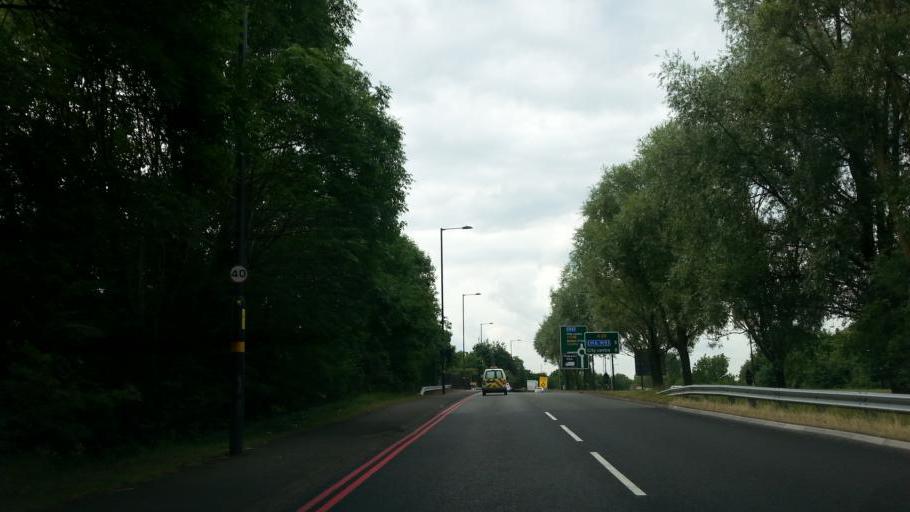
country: GB
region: England
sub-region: Warwickshire
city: Water Orton
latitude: 52.5295
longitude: -1.7771
